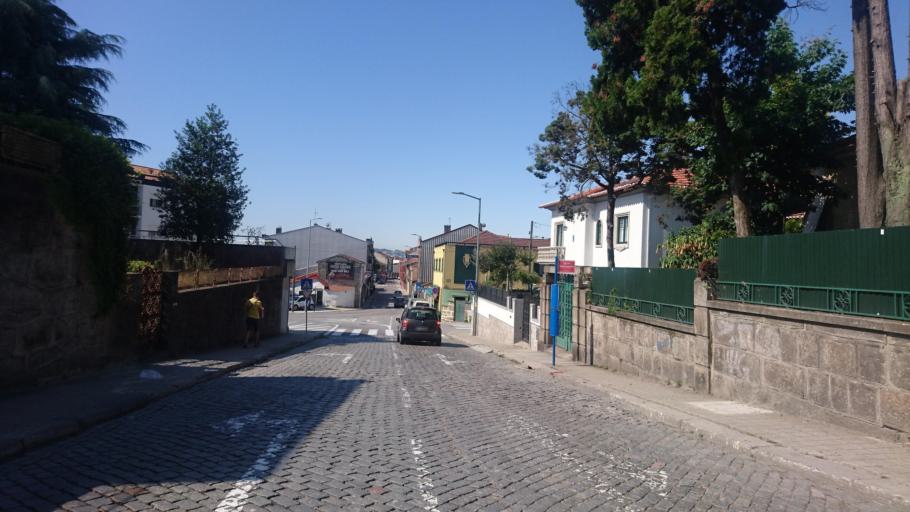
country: PT
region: Porto
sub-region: Gondomar
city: Rio Tinto
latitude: 41.1664
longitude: -8.5707
